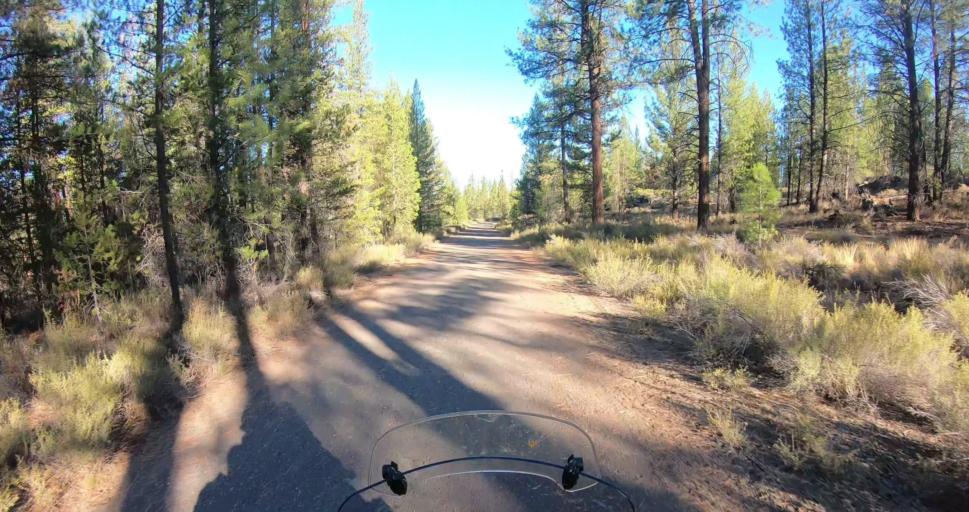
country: US
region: Oregon
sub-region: Deschutes County
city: La Pine
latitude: 43.7206
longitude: -121.4234
